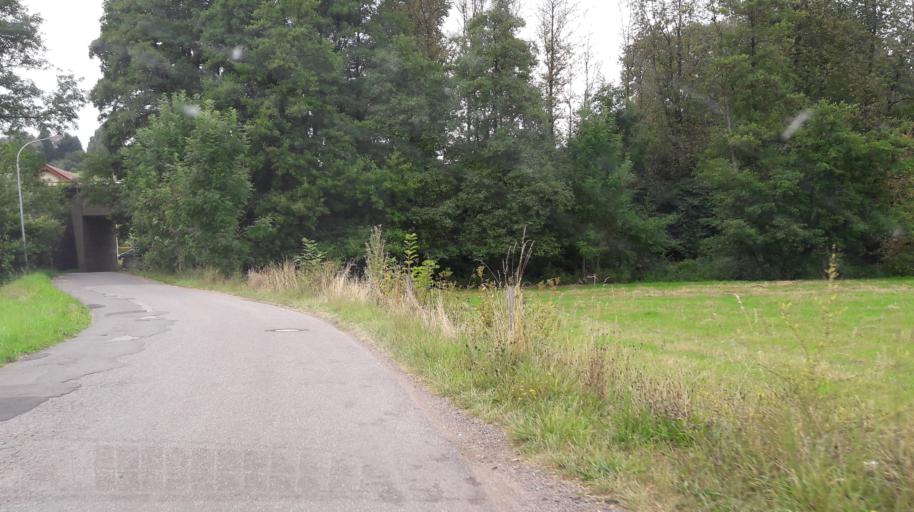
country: DE
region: Saarland
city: Sankt Wendel
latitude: 49.4790
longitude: 7.1751
